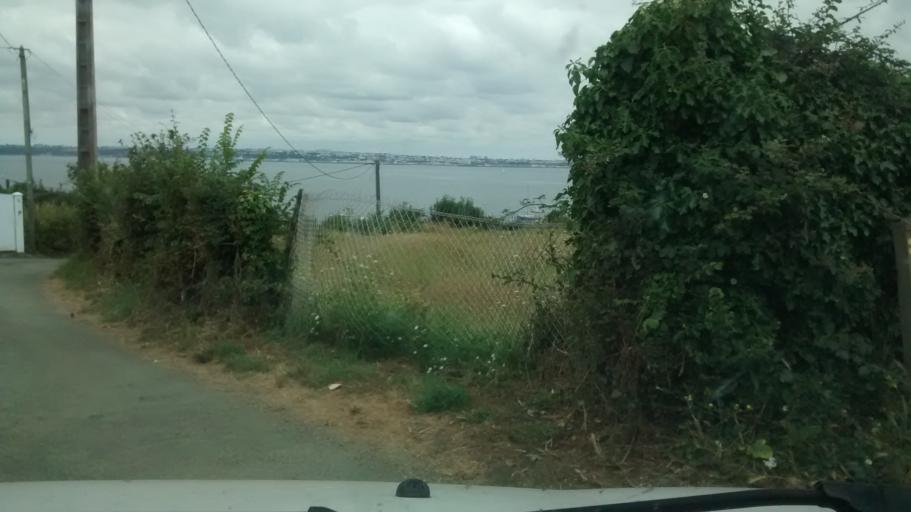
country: FR
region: Brittany
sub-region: Departement du Finistere
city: Lanveoc
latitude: 48.3291
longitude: -4.4488
